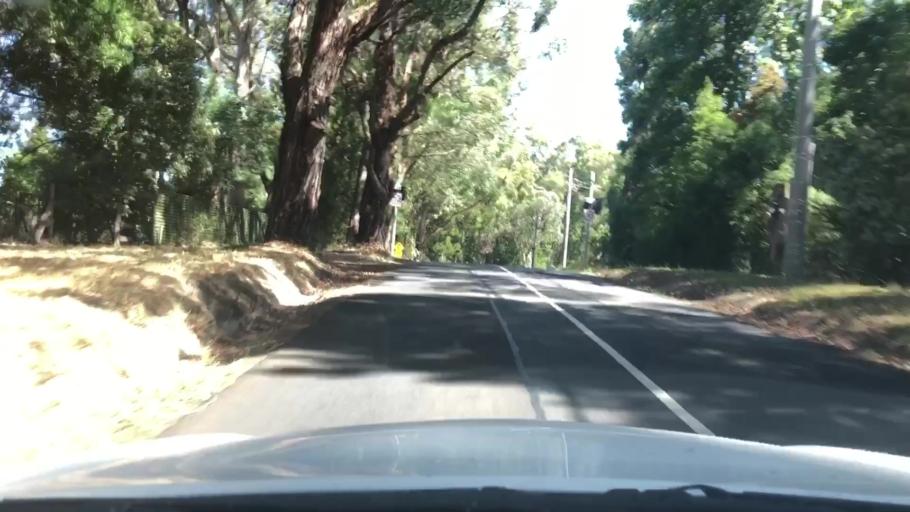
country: AU
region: Victoria
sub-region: Yarra Ranges
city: Macclesfield
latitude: -37.8908
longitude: 145.4756
